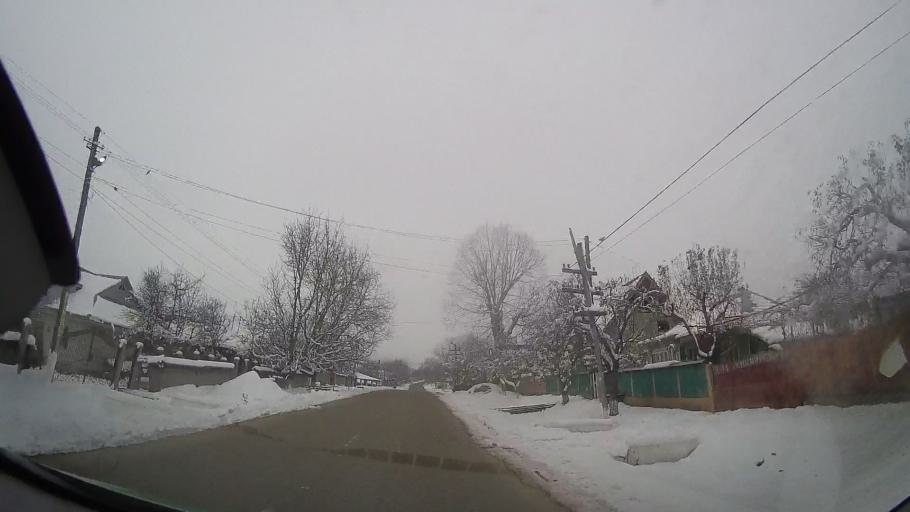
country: RO
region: Neamt
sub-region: Comuna Oniceni
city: Oniceni
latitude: 46.8084
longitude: 27.1852
